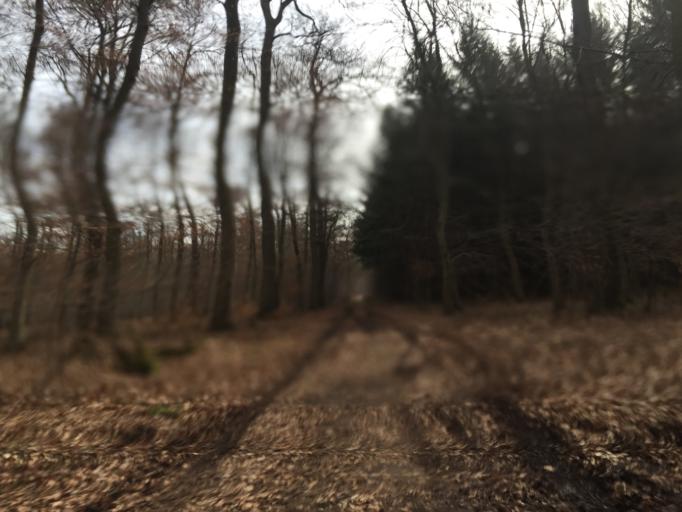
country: DE
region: Hesse
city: Viernheim
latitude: 49.5697
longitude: 8.5820
